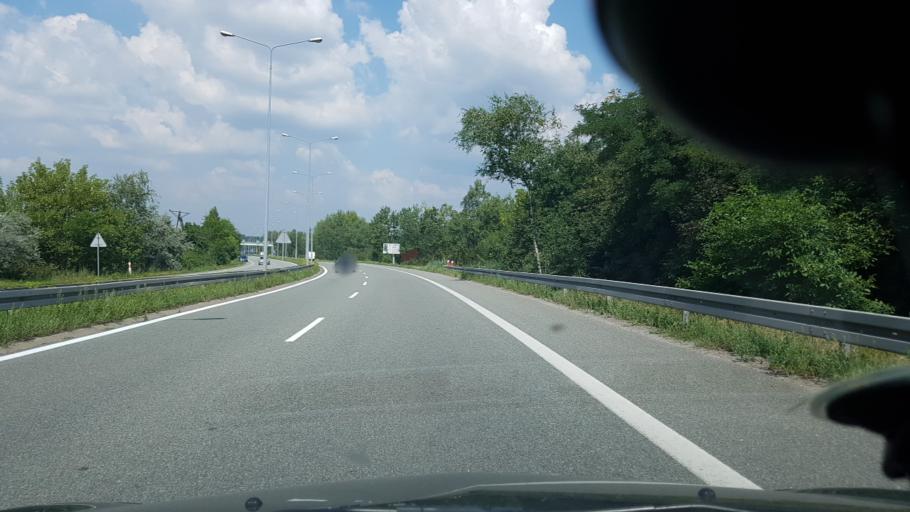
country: PL
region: Silesian Voivodeship
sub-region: Powiat mikolowski
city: Laziska Gorne
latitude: 50.1515
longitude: 18.8504
